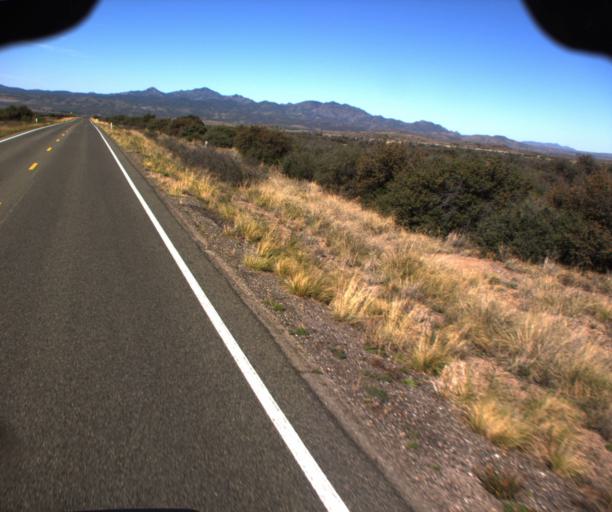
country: US
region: Arizona
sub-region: Yavapai County
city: Prescott
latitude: 34.3943
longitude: -112.6333
